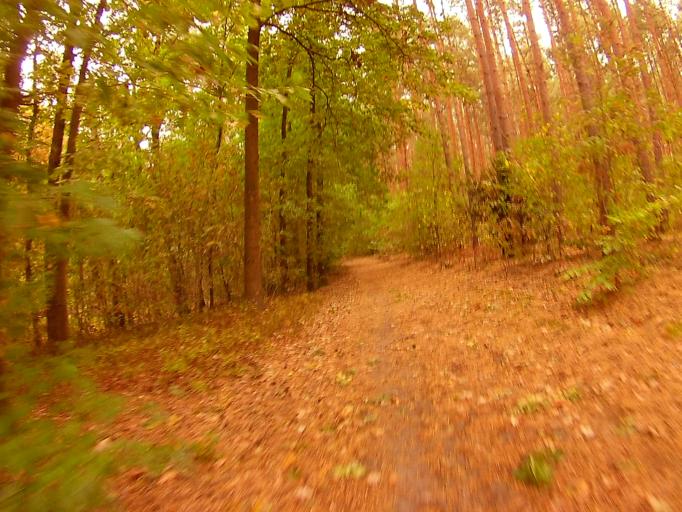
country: DE
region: Brandenburg
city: Zeuthen
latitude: 52.3931
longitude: 13.6255
